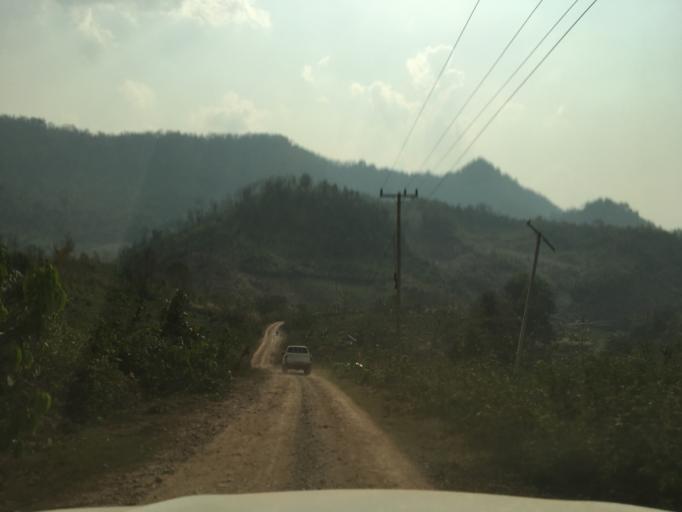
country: LA
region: Xiangkhoang
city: Phonsavan
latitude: 19.8201
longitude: 102.9997
